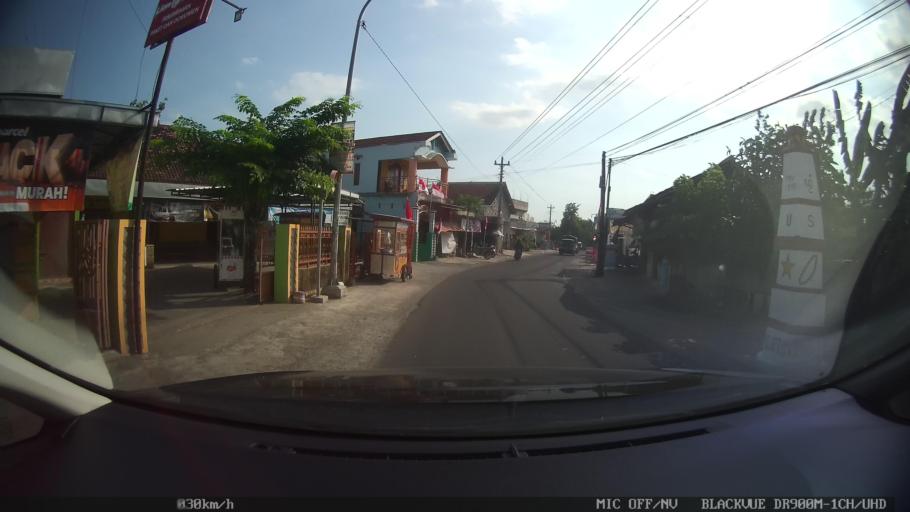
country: ID
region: Daerah Istimewa Yogyakarta
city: Kasihan
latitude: -7.8274
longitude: 110.3256
